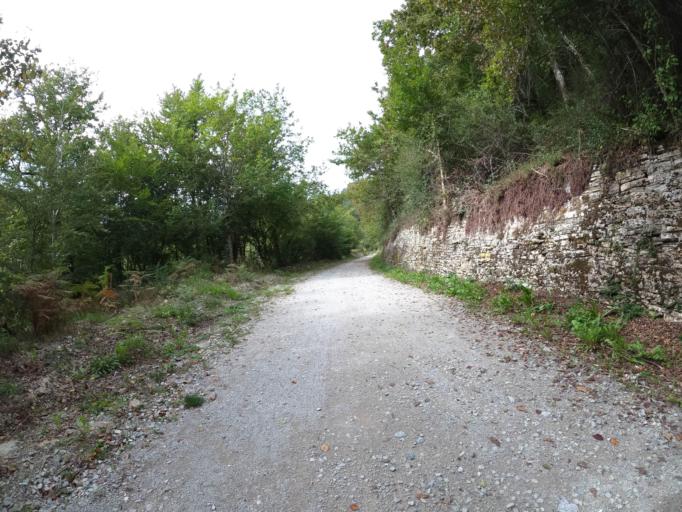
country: ES
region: Navarre
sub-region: Provincia de Navarra
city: Lekunberri
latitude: 42.9863
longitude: -1.8756
